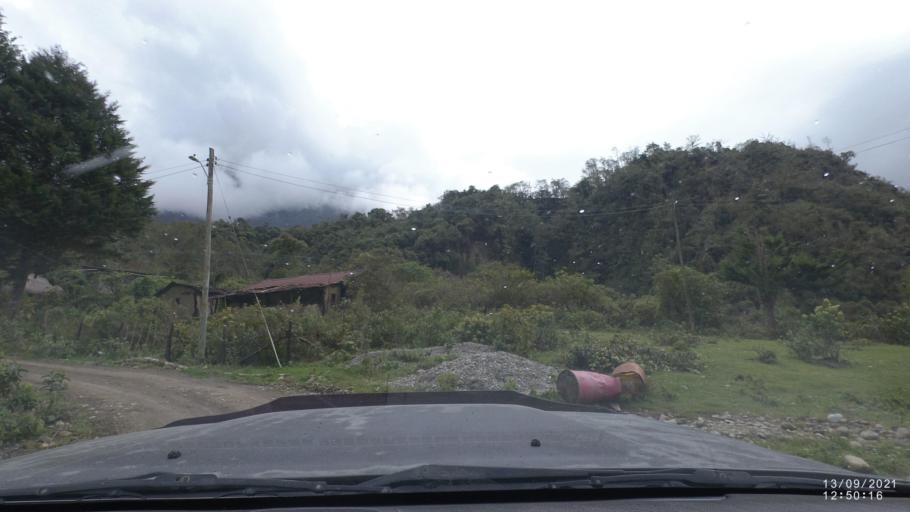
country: BO
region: Cochabamba
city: Colomi
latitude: -17.2364
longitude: -65.8186
